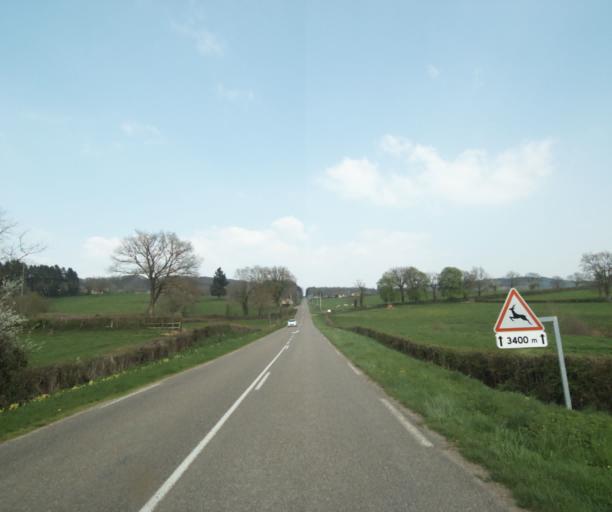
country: FR
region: Bourgogne
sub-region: Departement de Saone-et-Loire
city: Charolles
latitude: 46.4572
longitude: 4.3823
